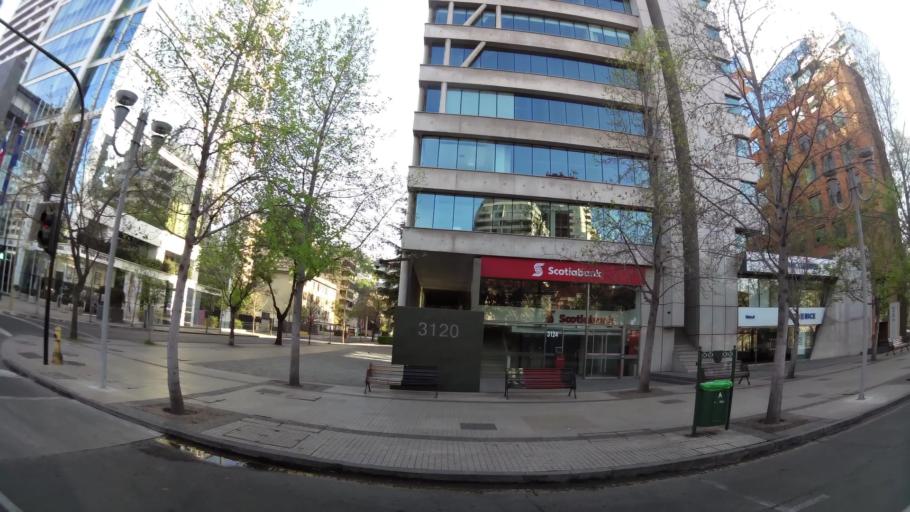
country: CL
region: Santiago Metropolitan
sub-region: Provincia de Santiago
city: Villa Presidente Frei, Nunoa, Santiago, Chile
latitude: -33.4143
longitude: -70.5978
